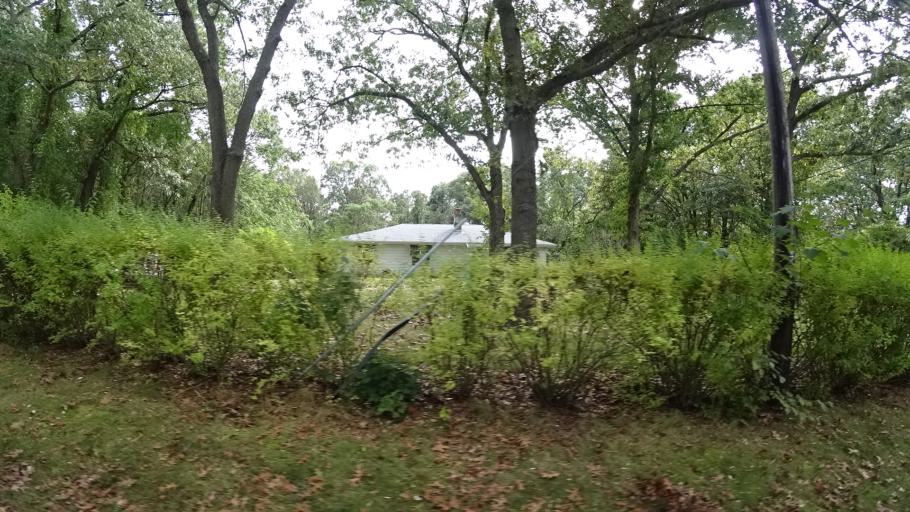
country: US
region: Indiana
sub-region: LaPorte County
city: Long Beach
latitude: 41.7331
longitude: -86.8466
